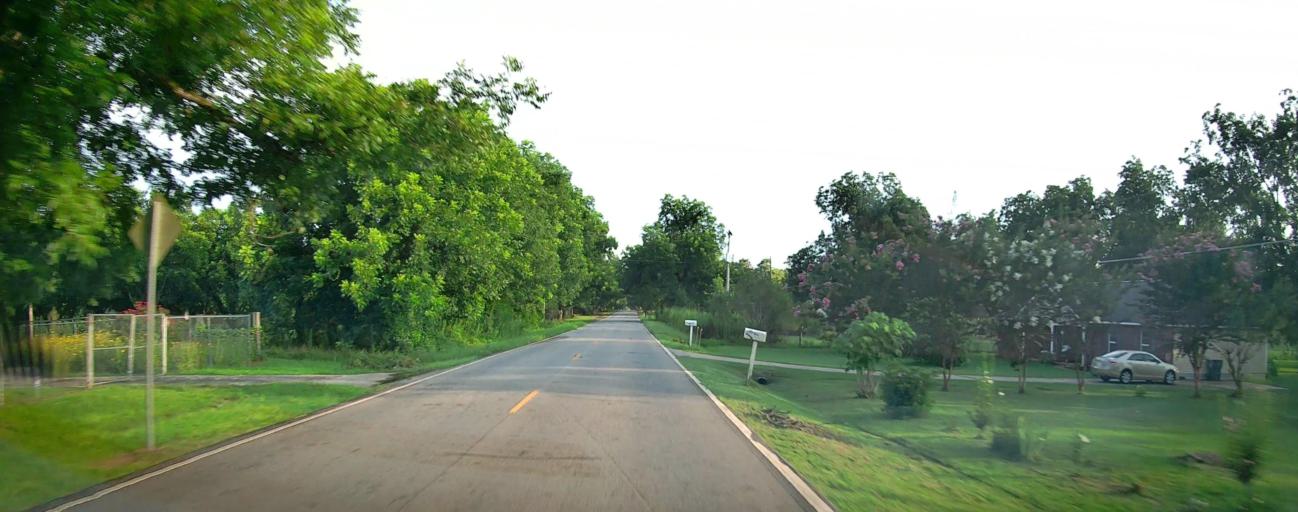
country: US
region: Georgia
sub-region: Peach County
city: Fort Valley
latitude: 32.5836
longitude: -83.8738
